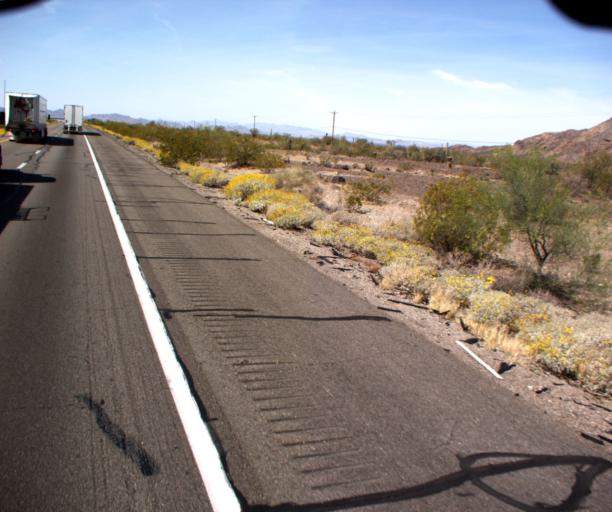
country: US
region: Arizona
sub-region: La Paz County
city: Quartzsite
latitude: 33.6791
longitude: -114.0751
